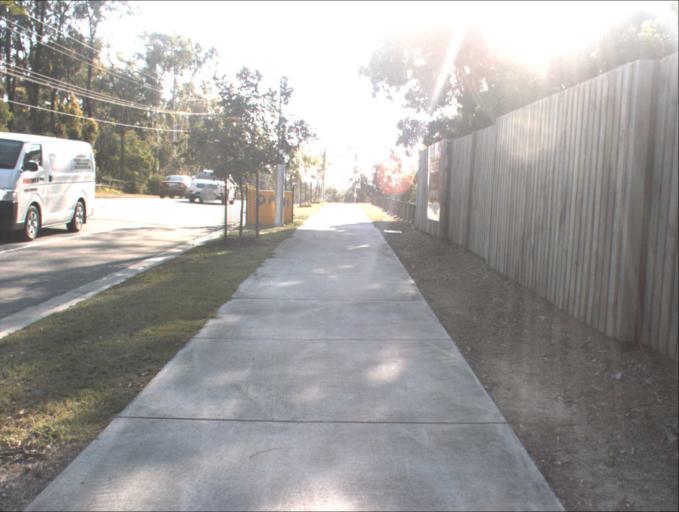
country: AU
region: Queensland
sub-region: Logan
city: Park Ridge South
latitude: -27.6887
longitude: 153.0462
